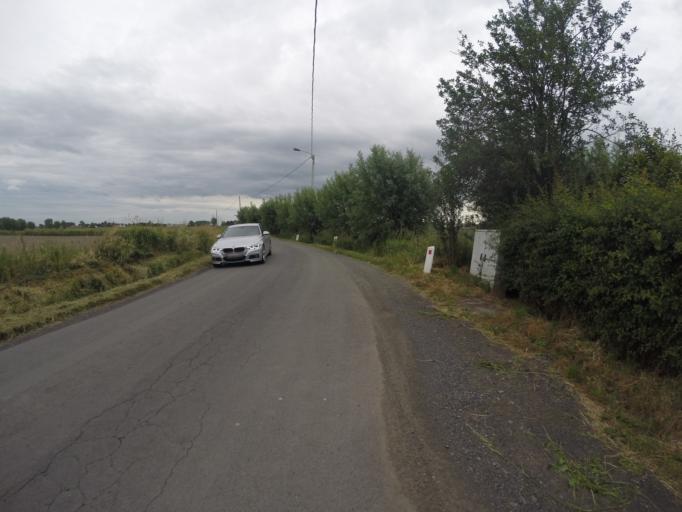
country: BE
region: Flanders
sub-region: Provincie West-Vlaanderen
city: Ruiselede
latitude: 51.0624
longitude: 3.3577
